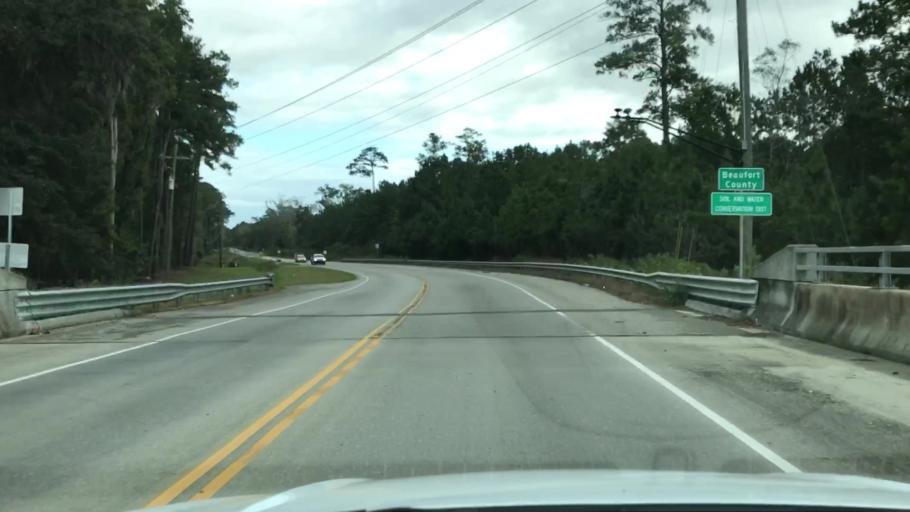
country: US
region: South Carolina
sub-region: Jasper County
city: Hardeeville
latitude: 32.2364
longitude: -81.0119
